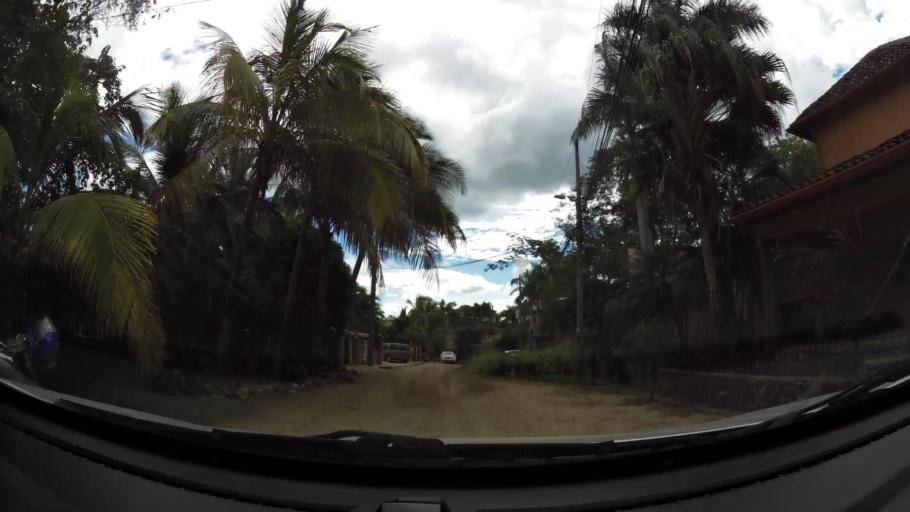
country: CR
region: Guanacaste
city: Santa Cruz
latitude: 10.2948
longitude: -85.8375
